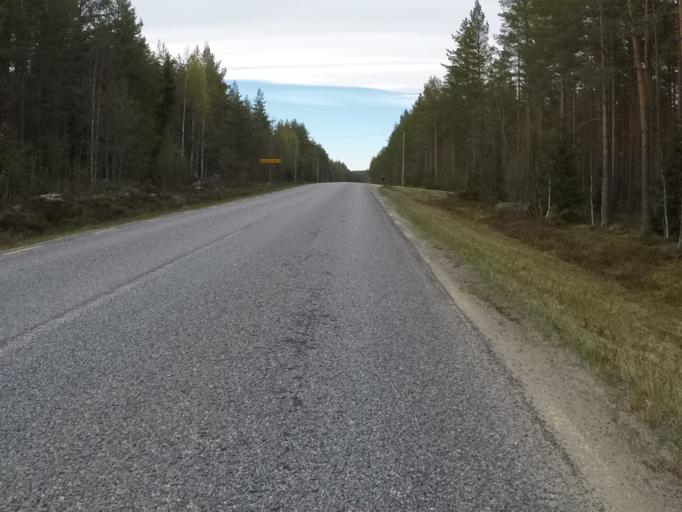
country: SE
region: Vaesterbotten
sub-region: Umea Kommun
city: Saevar
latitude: 63.9454
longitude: 20.7899
